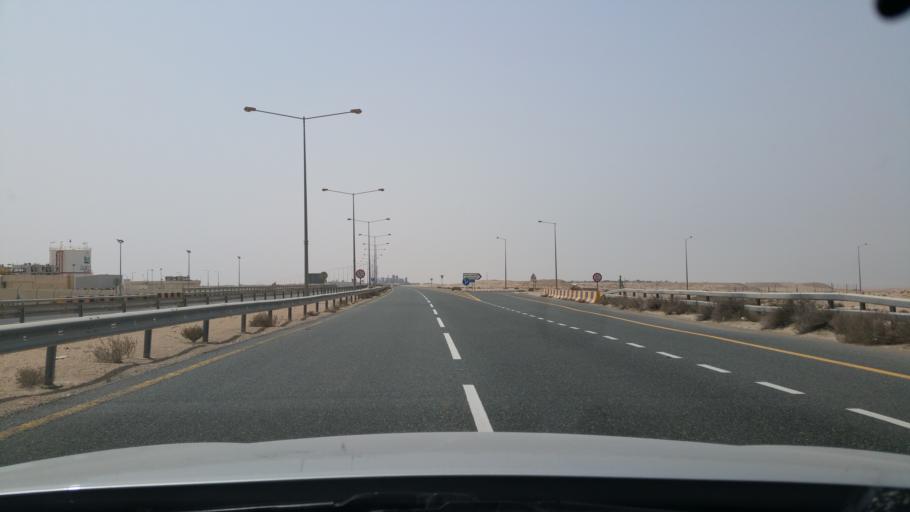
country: QA
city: Umm Bab
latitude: 25.2339
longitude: 50.8017
